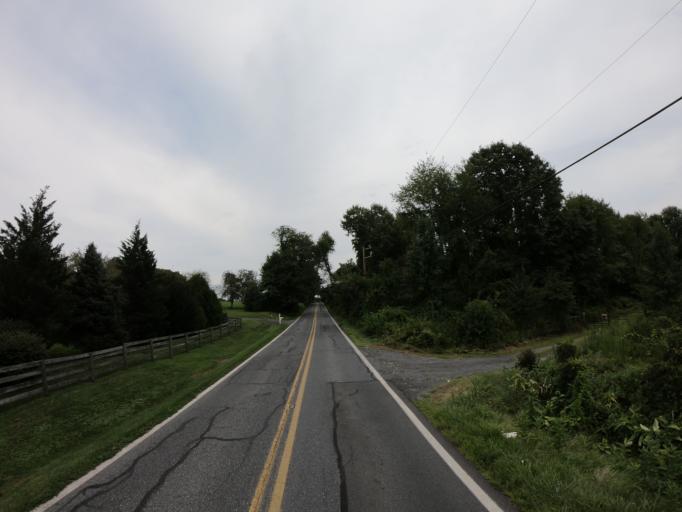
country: US
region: Maryland
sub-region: Montgomery County
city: Olney
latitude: 39.2203
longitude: -77.0917
